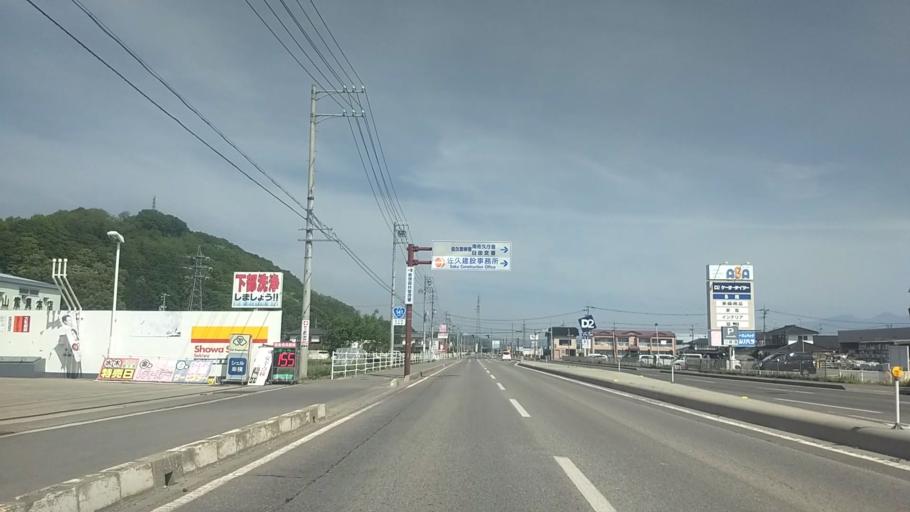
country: JP
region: Nagano
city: Saku
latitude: 36.1969
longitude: 138.4746
